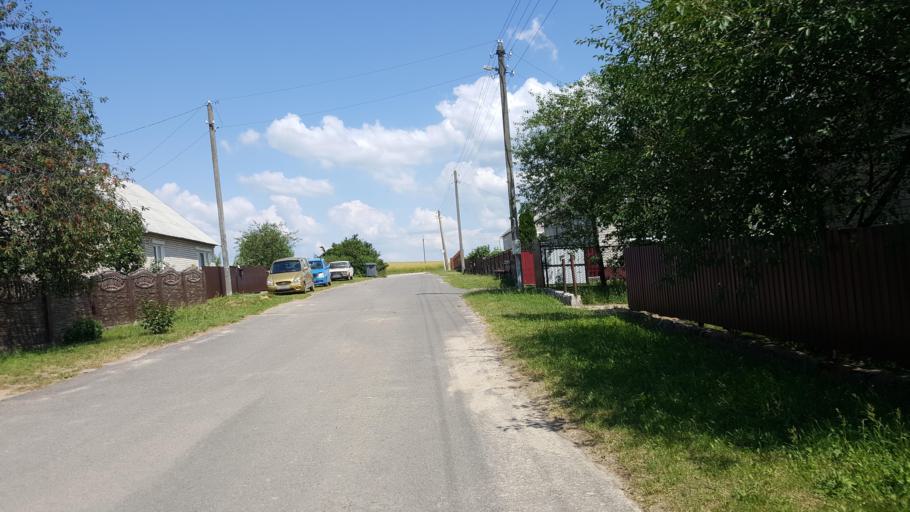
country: BY
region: Brest
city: Kamyanyets
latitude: 52.4092
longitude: 23.8358
